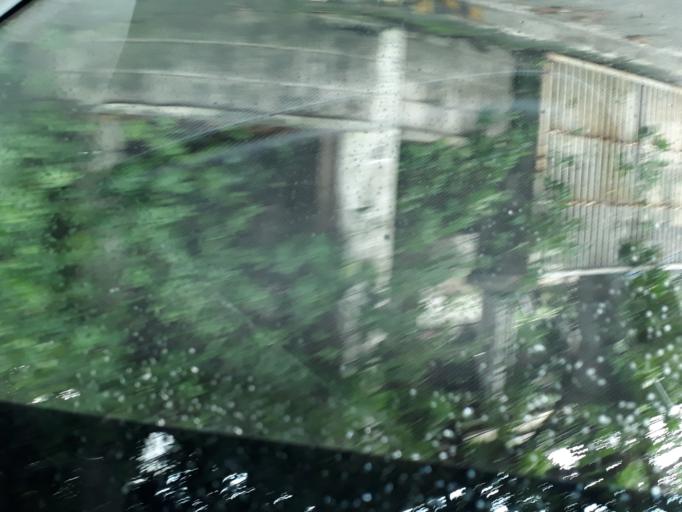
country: PH
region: Metro Manila
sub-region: Caloocan City
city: Niugan
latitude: 14.6665
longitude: 120.9866
